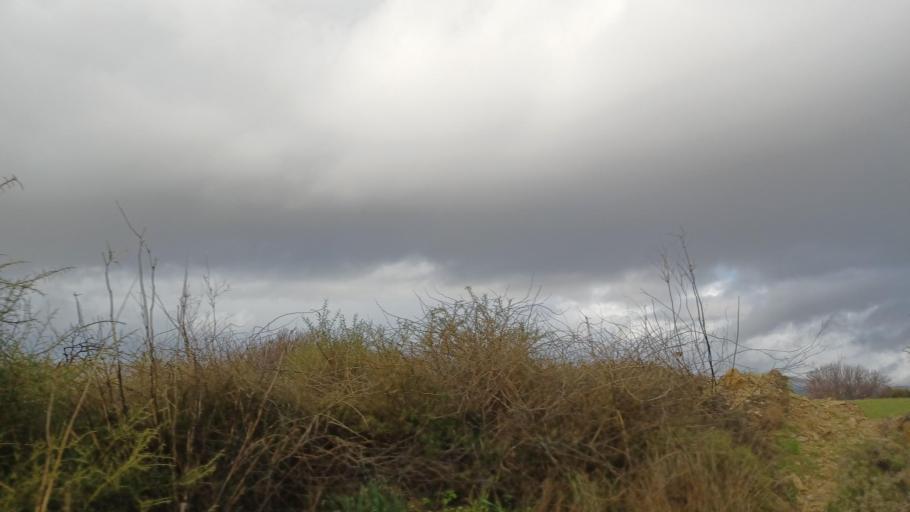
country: CY
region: Limassol
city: Pachna
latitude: 34.8303
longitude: 32.7442
